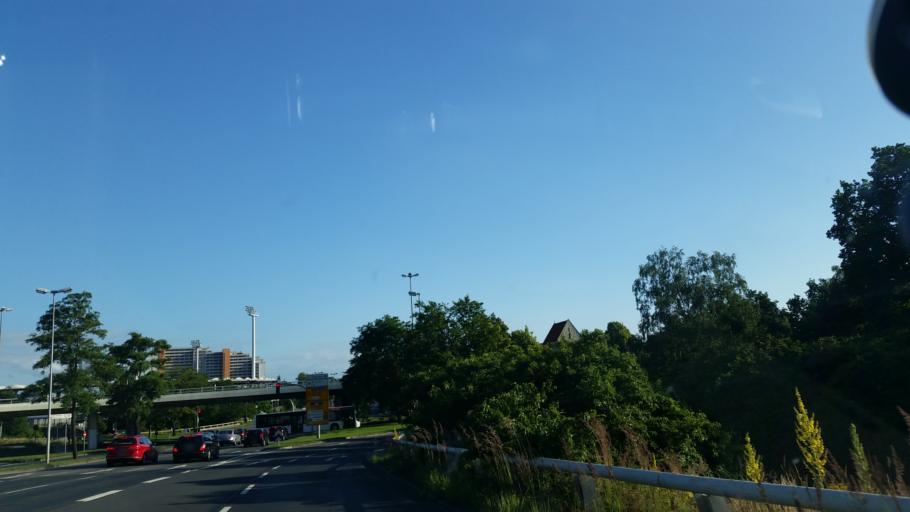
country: DE
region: Lower Saxony
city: Wolfsburg
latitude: 52.4284
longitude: 10.7990
